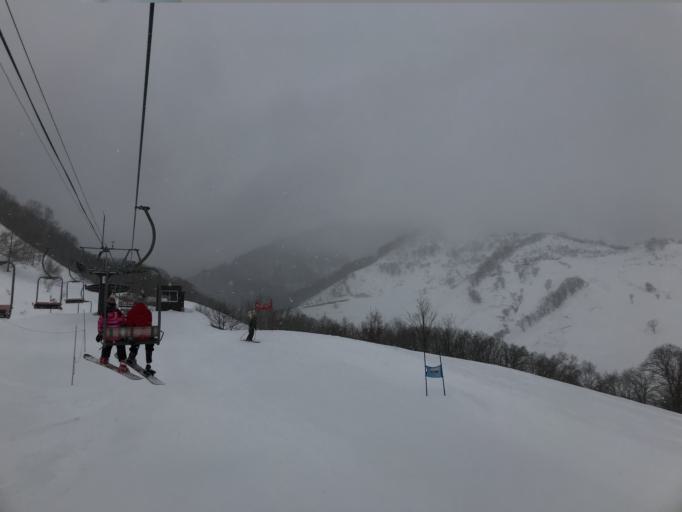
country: JP
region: Nagano
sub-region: Kitaazumi Gun
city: Hakuba
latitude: 36.7598
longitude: 137.8619
